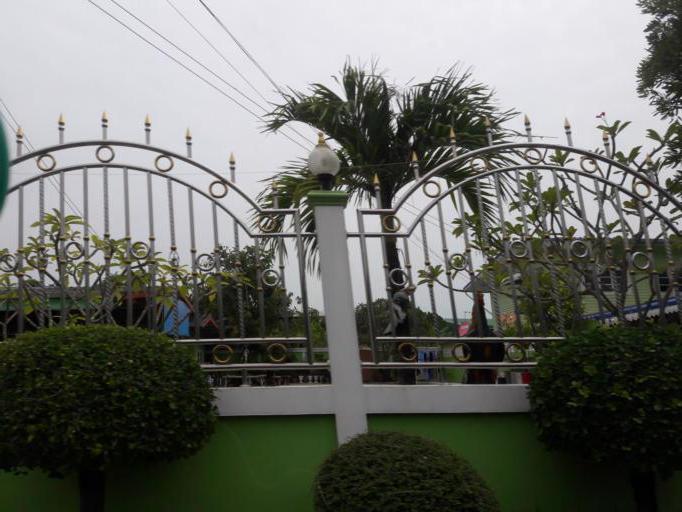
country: TH
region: Ratchaburi
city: Damnoen Saduak
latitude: 13.5137
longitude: 99.9913
